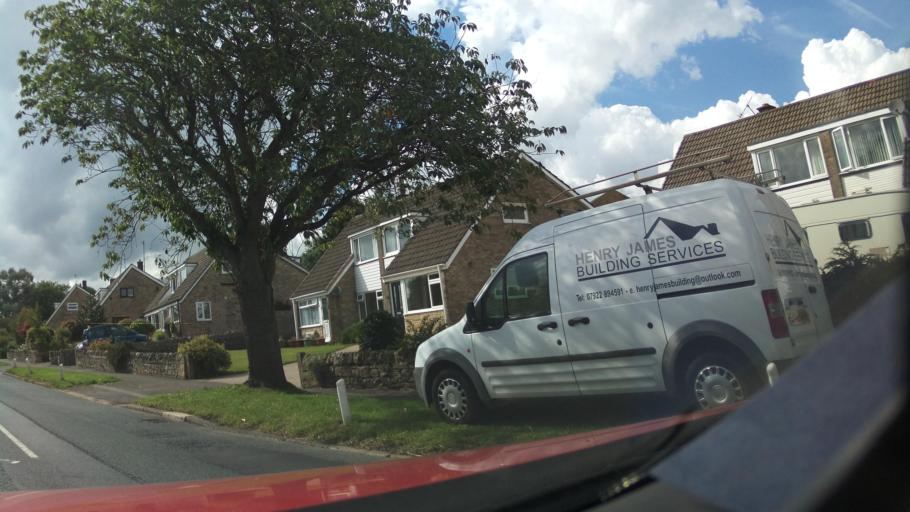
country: GB
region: England
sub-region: North Yorkshire
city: Catterick Garrison
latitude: 54.4096
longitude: -1.7198
